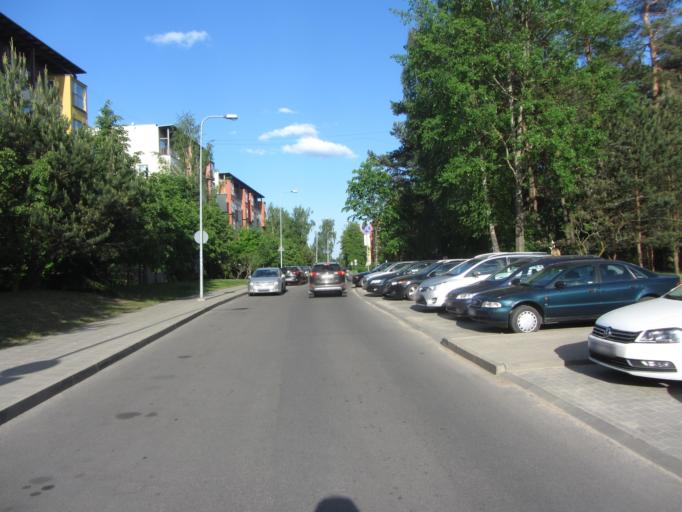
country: LT
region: Vilnius County
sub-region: Vilnius
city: Fabijoniskes
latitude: 54.7418
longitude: 25.2657
